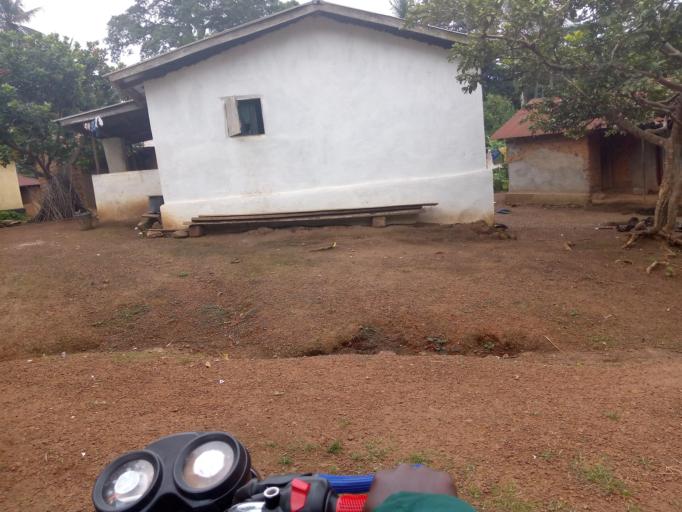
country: SL
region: Eastern Province
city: Buedu
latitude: 8.4808
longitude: -10.3272
